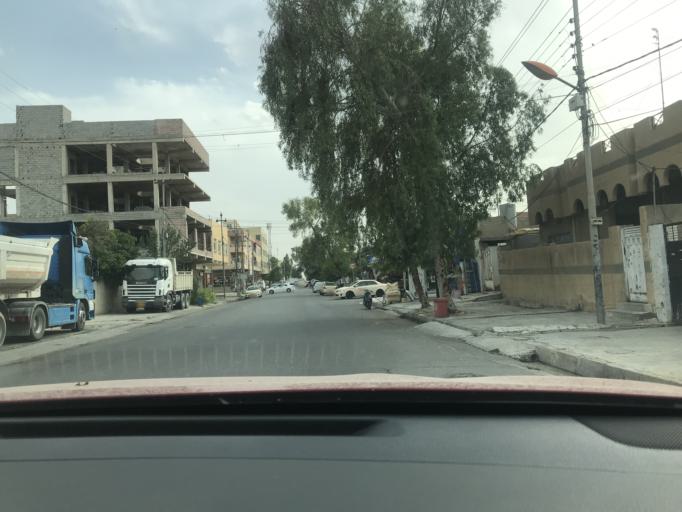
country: IQ
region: Arbil
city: Erbil
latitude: 36.1773
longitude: 43.9757
